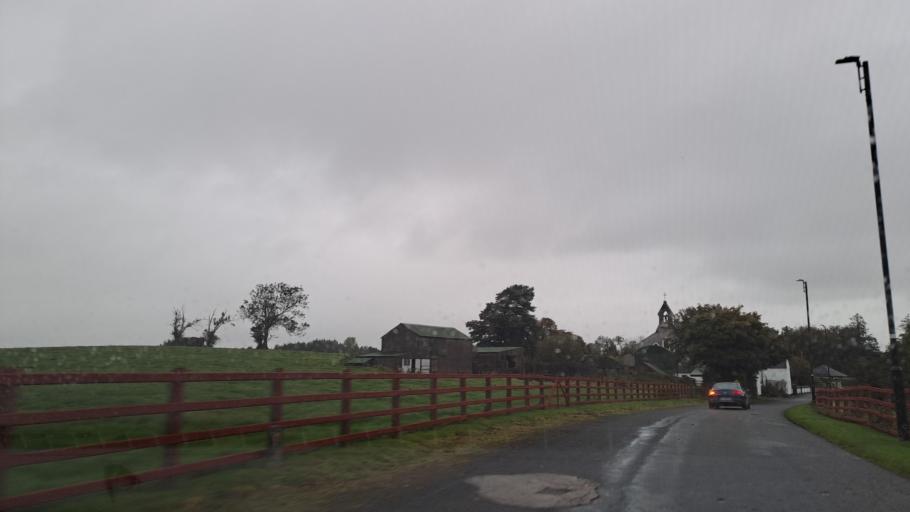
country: IE
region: Ulster
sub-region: County Monaghan
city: Monaghan
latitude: 54.2116
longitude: -6.9091
